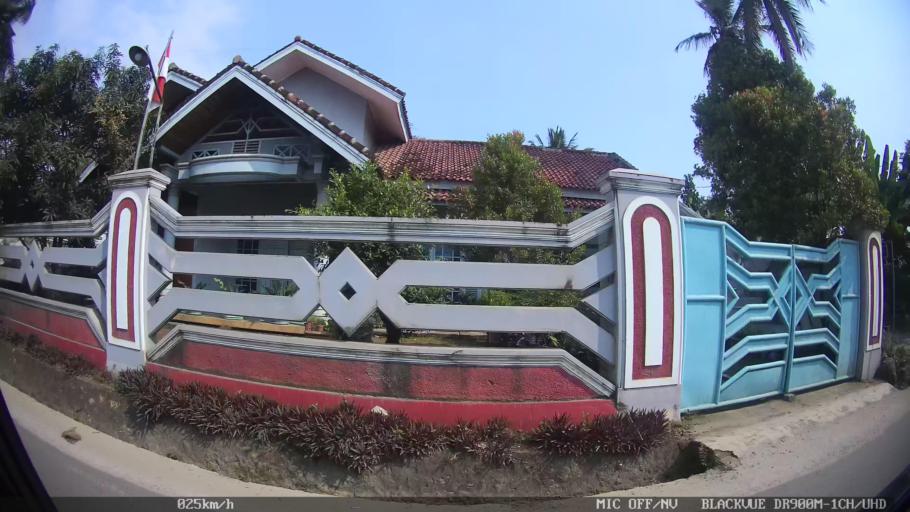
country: ID
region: Lampung
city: Natar
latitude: -5.3484
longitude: 105.2200
